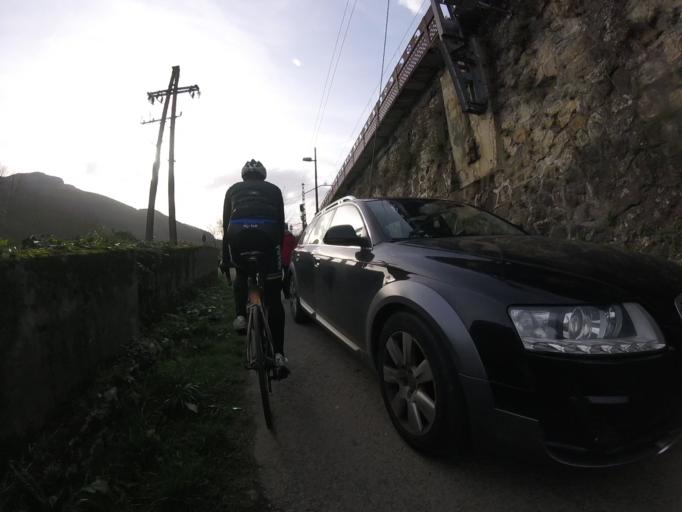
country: ES
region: Basque Country
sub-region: Provincia de Guipuzcoa
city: Anoeta
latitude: 43.1654
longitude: -2.0717
